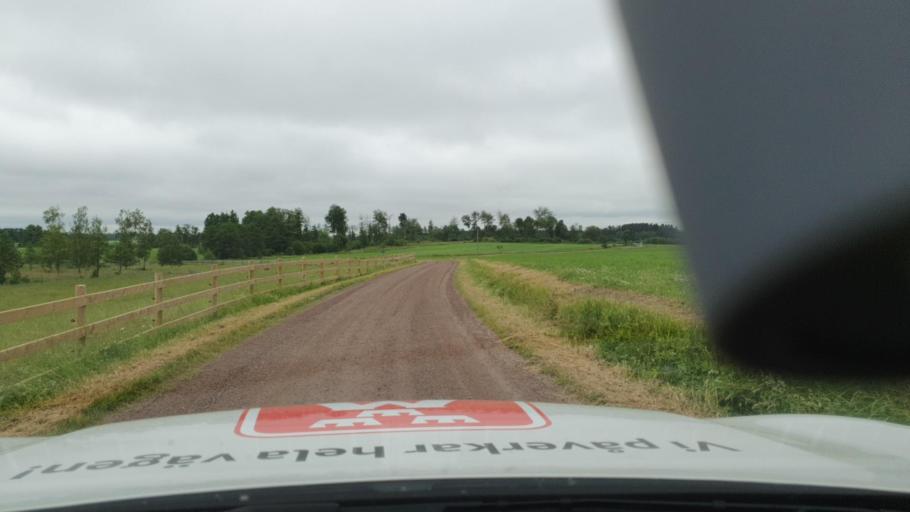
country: SE
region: Vaestra Goetaland
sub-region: Tidaholms Kommun
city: Olofstorp
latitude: 58.3978
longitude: 14.0004
